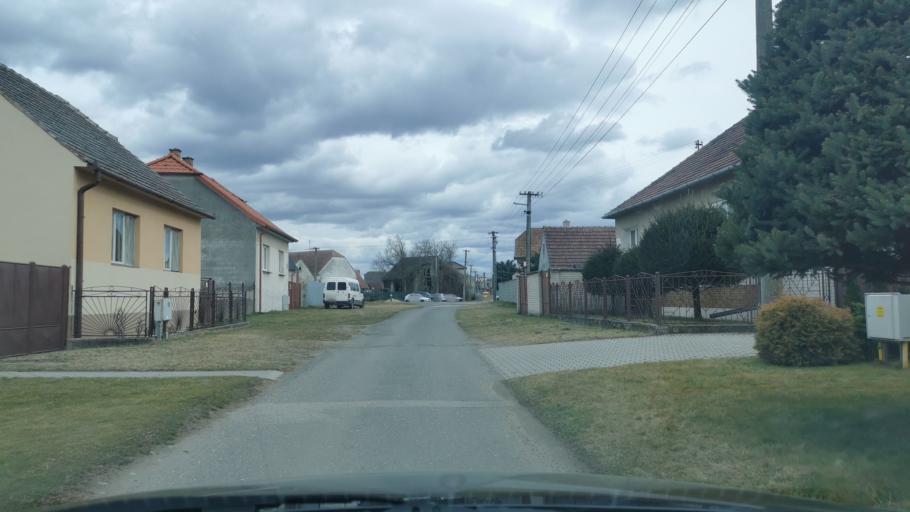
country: CZ
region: South Moravian
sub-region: Okres Breclav
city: Lanzhot
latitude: 48.6884
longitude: 17.0048
